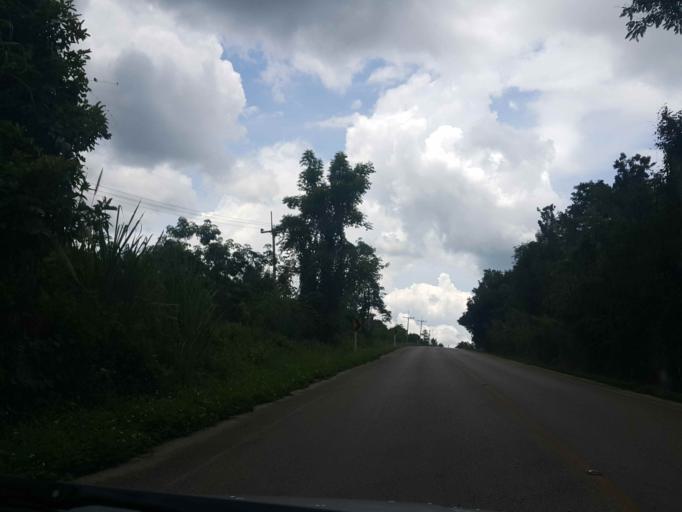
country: TH
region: Lampang
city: Ngao
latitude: 18.9401
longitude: 100.0778
